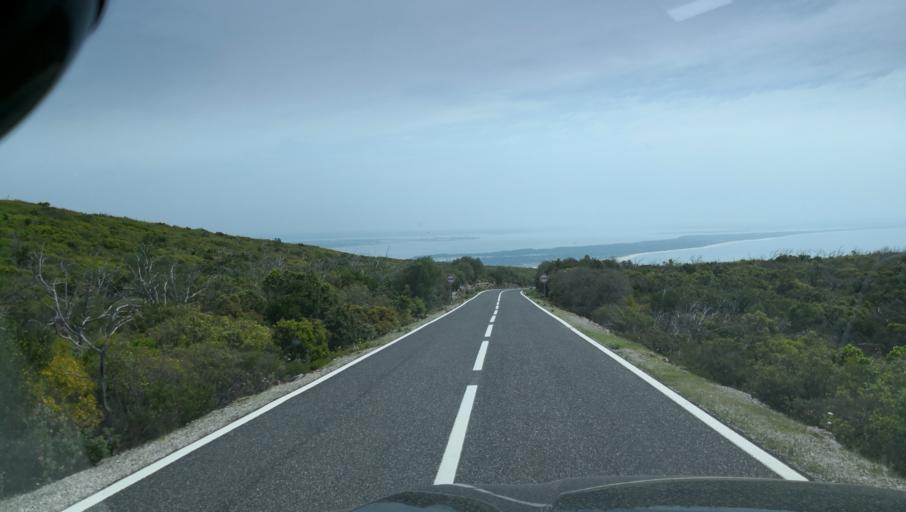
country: PT
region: Setubal
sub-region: Setubal
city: Setubal
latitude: 38.4897
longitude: -8.9524
